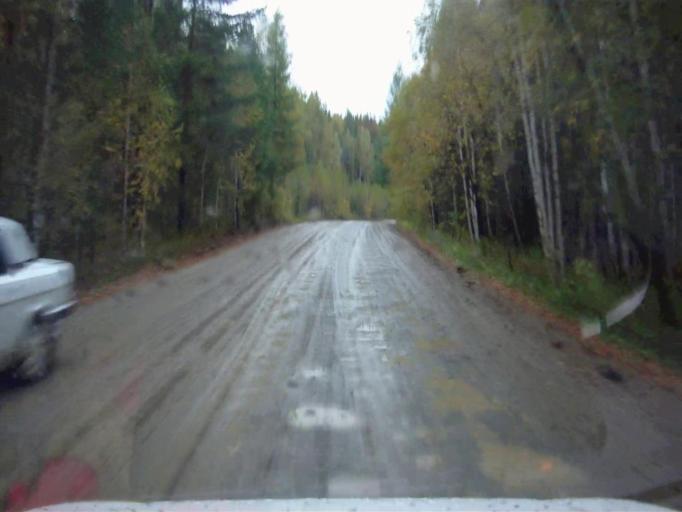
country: RU
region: Chelyabinsk
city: Kyshtym
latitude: 55.7499
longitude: 60.4876
